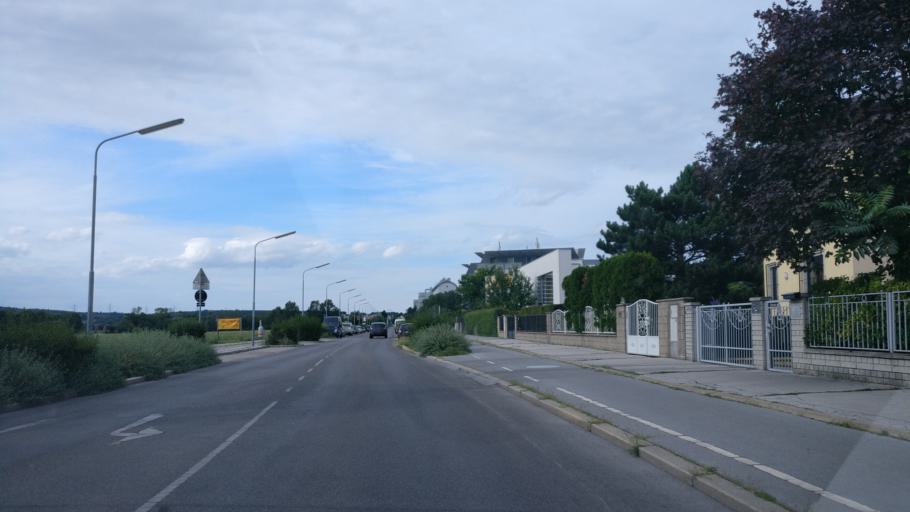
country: AT
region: Lower Austria
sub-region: Politischer Bezirk Korneuburg
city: Hagenbrunn
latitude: 48.2855
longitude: 16.4098
